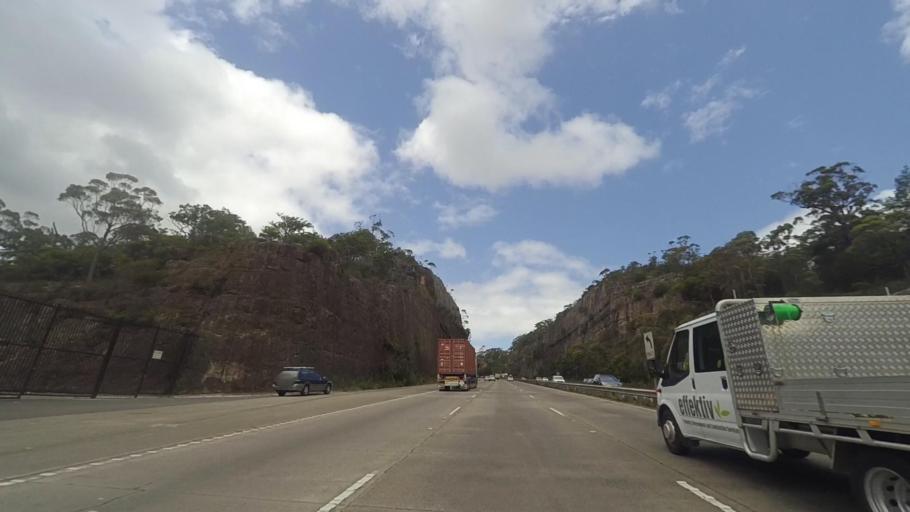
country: AU
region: New South Wales
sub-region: Gosford Shire
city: Point Clare
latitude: -33.4340
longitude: 151.2580
